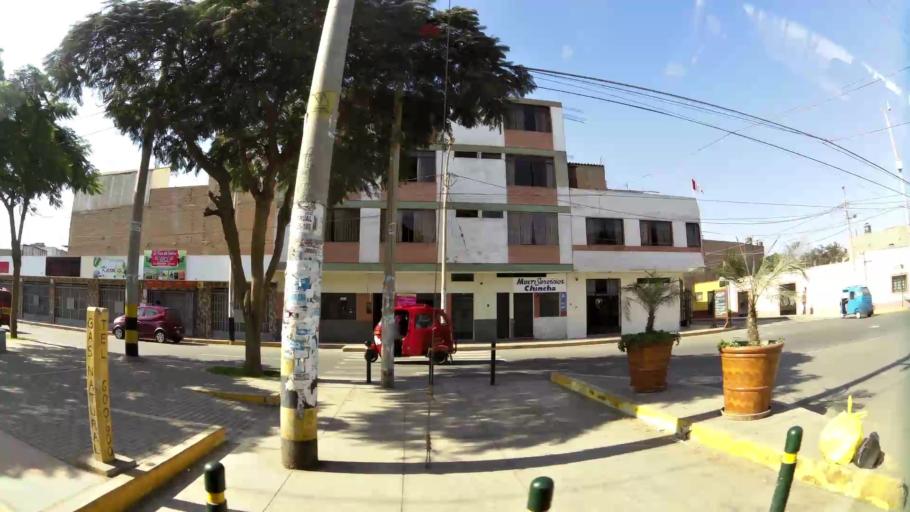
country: PE
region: Ica
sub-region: Provincia de Chincha
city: Chincha Alta
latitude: -13.4199
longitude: -76.1354
